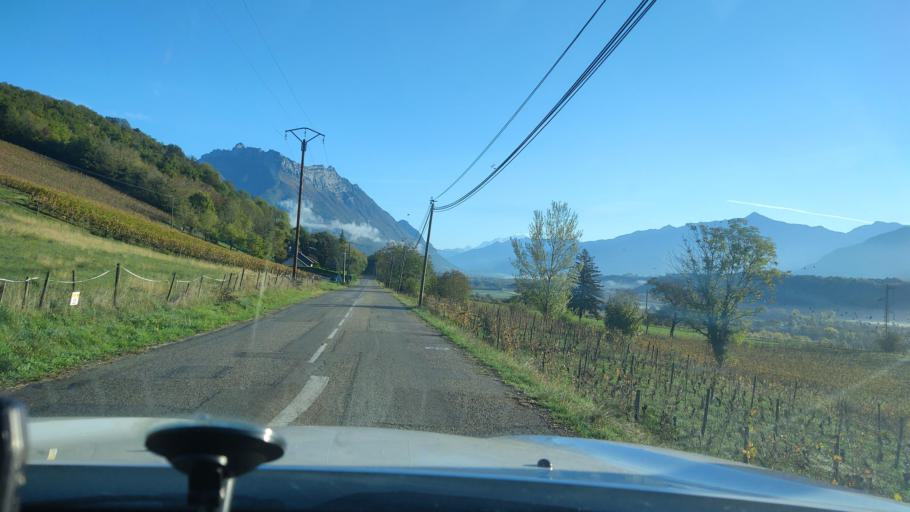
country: FR
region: Rhone-Alpes
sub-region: Departement de la Savoie
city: Cruet
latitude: 45.5295
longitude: 6.0972
